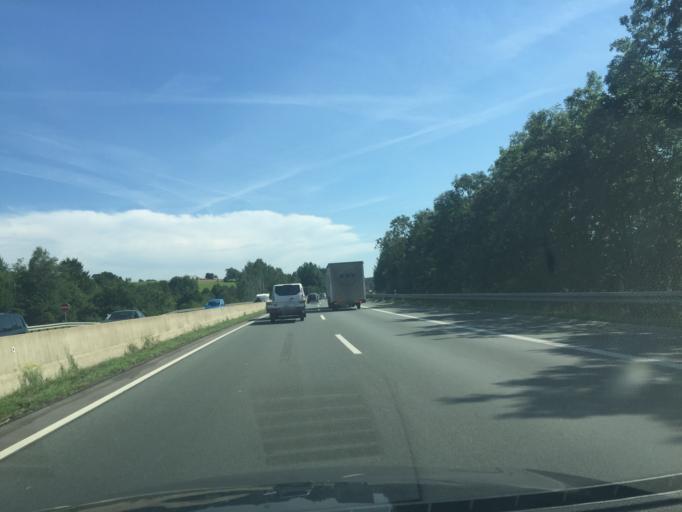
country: DE
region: North Rhine-Westphalia
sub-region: Regierungsbezirk Arnsberg
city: Wenden
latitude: 50.9441
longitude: 7.8762
